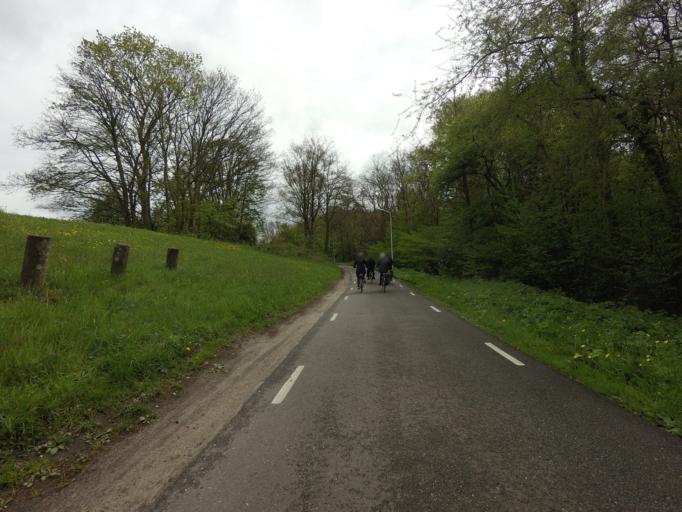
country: NL
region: North Holland
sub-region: Gemeente Naarden
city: Naarden
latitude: 52.3301
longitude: 5.1092
